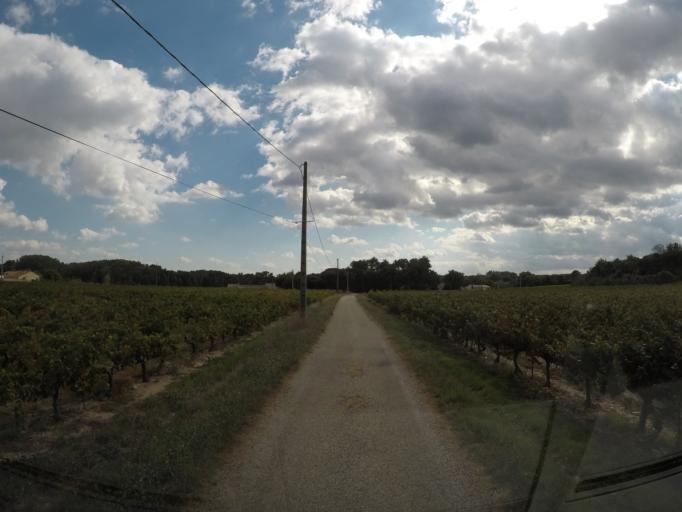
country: FR
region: Rhone-Alpes
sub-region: Departement de la Drome
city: Suze-la-Rousse
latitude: 44.2942
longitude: 4.8126
